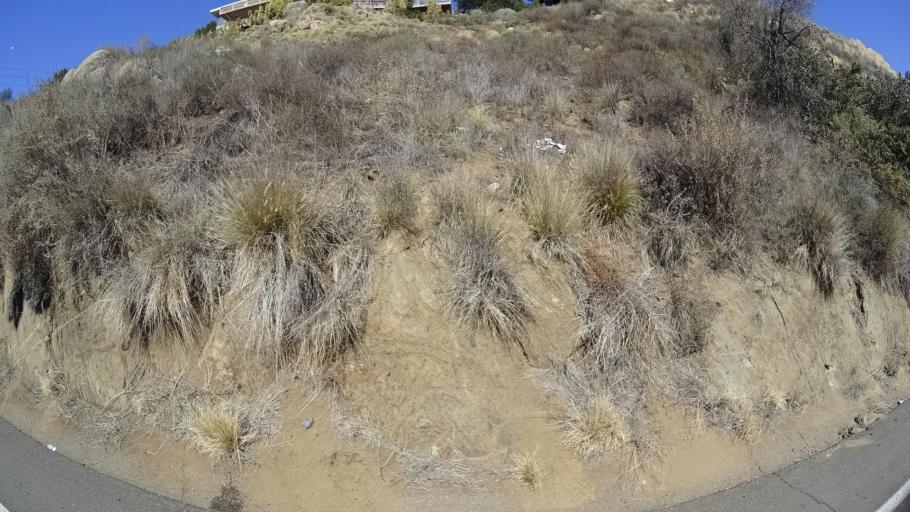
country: US
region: California
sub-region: San Diego County
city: Granite Hills
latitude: 32.7852
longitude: -116.8913
